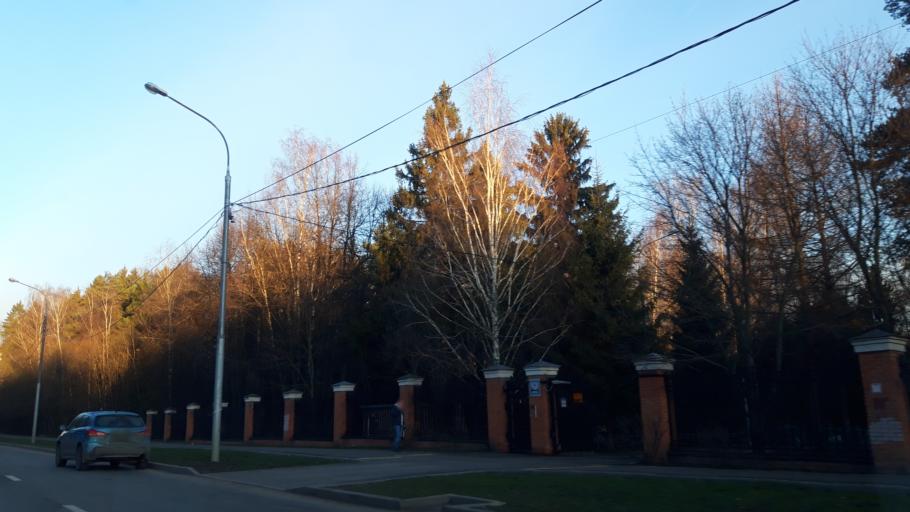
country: RU
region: Moskovskaya
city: Rzhavki
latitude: 55.9953
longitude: 37.2416
